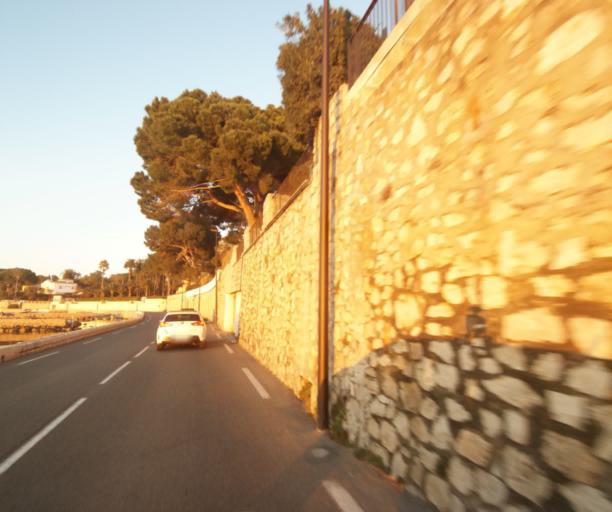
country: FR
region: Provence-Alpes-Cote d'Azur
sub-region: Departement des Alpes-Maritimes
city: Antibes
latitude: 43.5563
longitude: 7.1216
